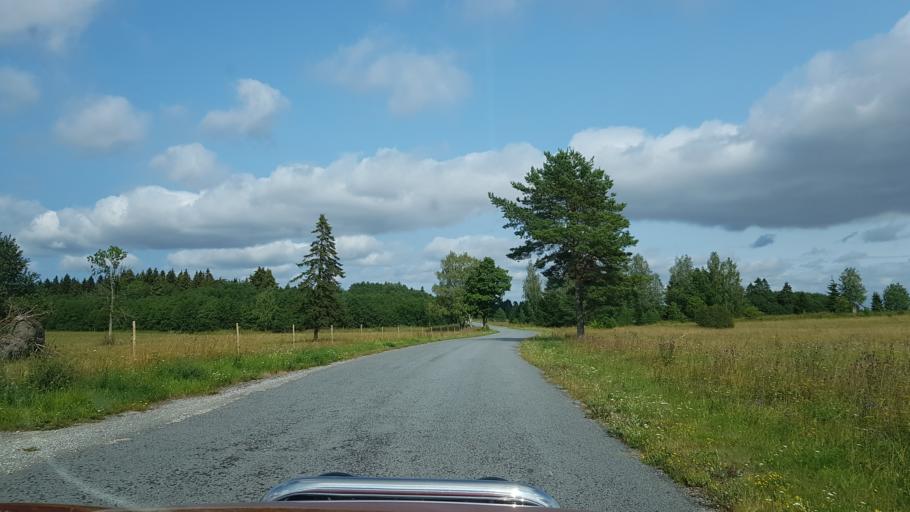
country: EE
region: Laeaene-Virumaa
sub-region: Tapa vald
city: Tapa
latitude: 59.3278
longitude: 26.0300
